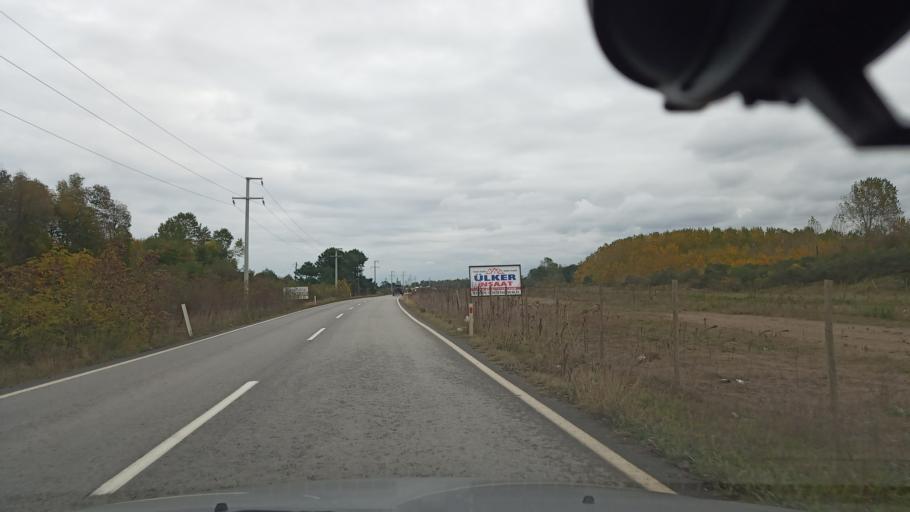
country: TR
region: Sakarya
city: Karasu
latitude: 41.1204
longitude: 30.5974
